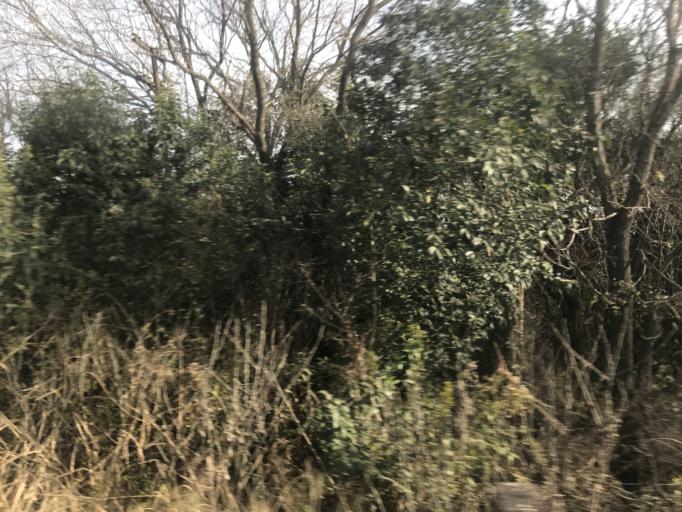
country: AR
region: Cordoba
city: Laguna Larga
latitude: -31.7837
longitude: -63.7972
